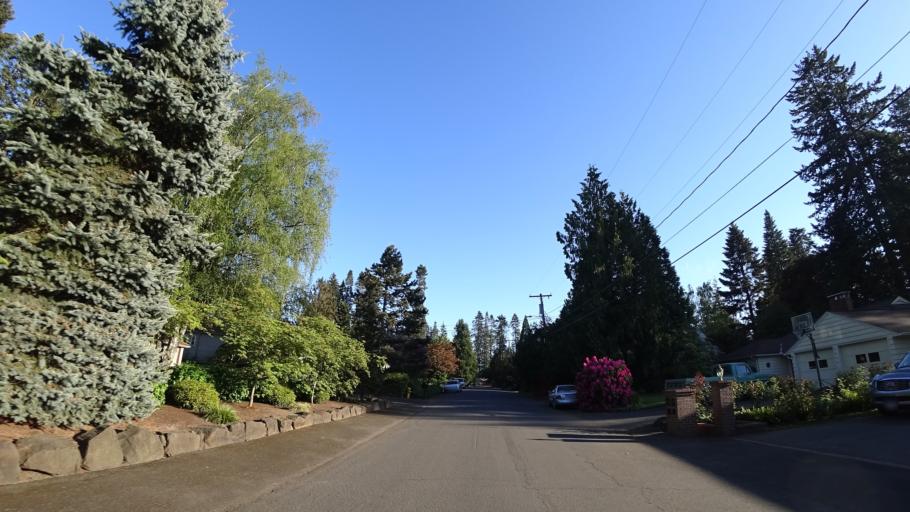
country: US
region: Oregon
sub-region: Washington County
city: West Slope
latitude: 45.4897
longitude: -122.7652
